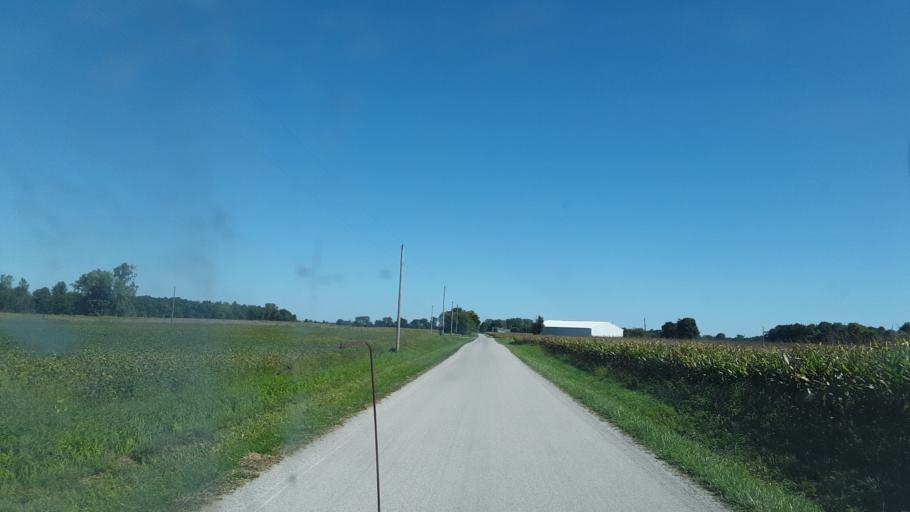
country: US
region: Ohio
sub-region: Wyandot County
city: Upper Sandusky
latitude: 40.9326
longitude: -83.2423
